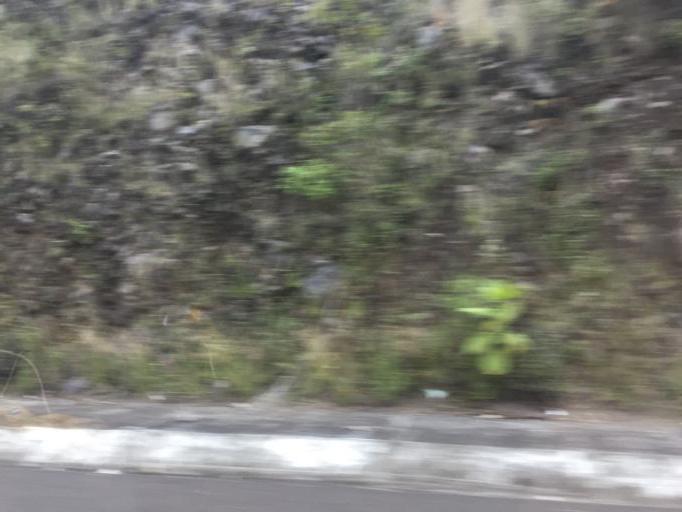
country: MX
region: Michoacan
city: Panindicuaro de la Reforma
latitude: 19.9731
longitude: -101.7307
